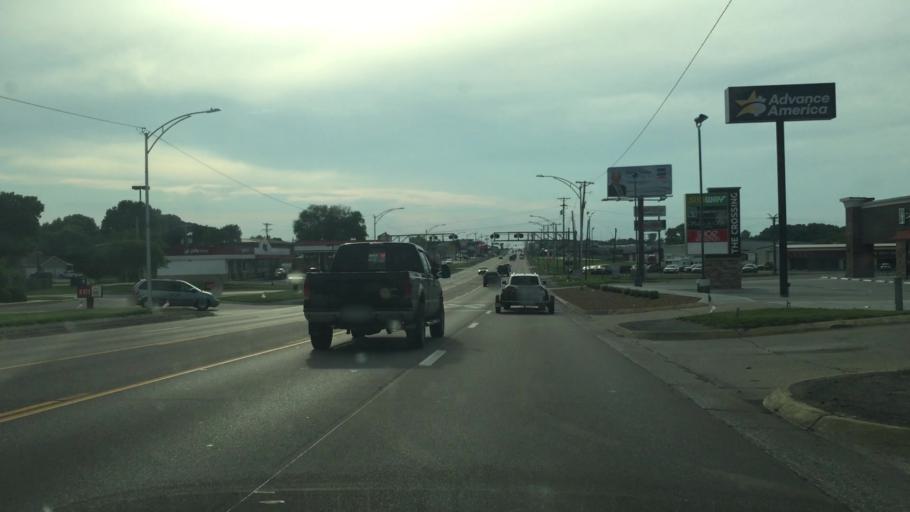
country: US
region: Missouri
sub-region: Pettis County
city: Sedalia
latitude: 38.7061
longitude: -93.2583
